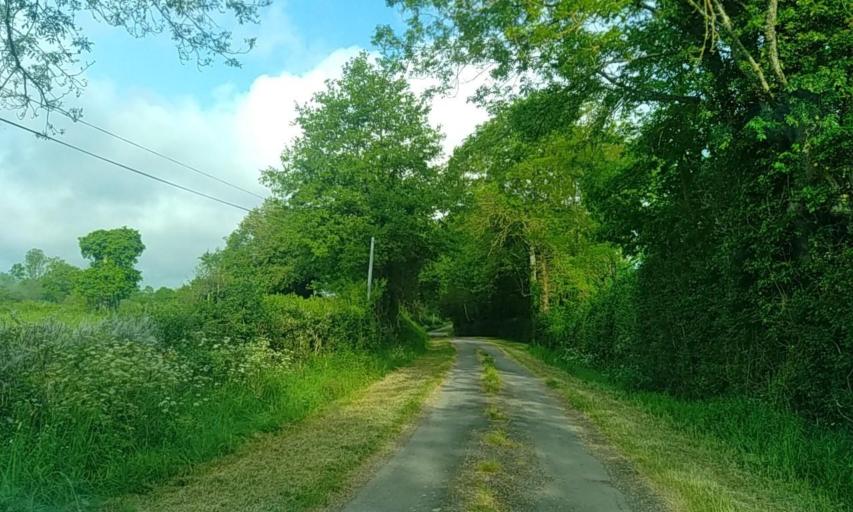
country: FR
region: Poitou-Charentes
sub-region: Departement des Deux-Sevres
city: Boisme
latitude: 46.7598
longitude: -0.4377
